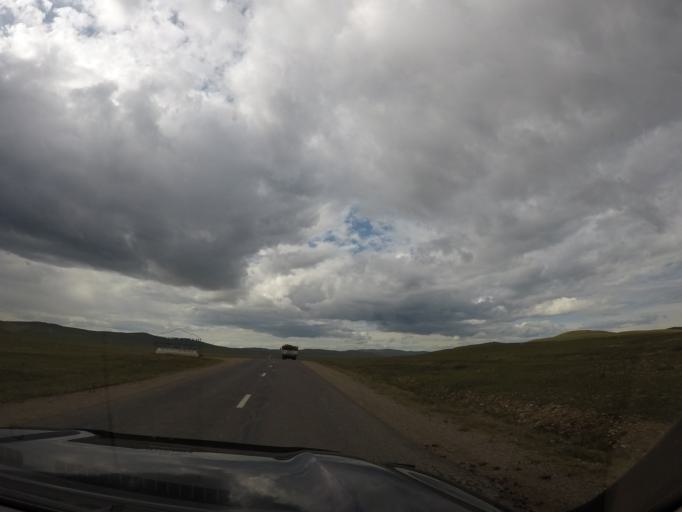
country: MN
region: Hentiy
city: Avraga
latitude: 47.5068
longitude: 109.4363
